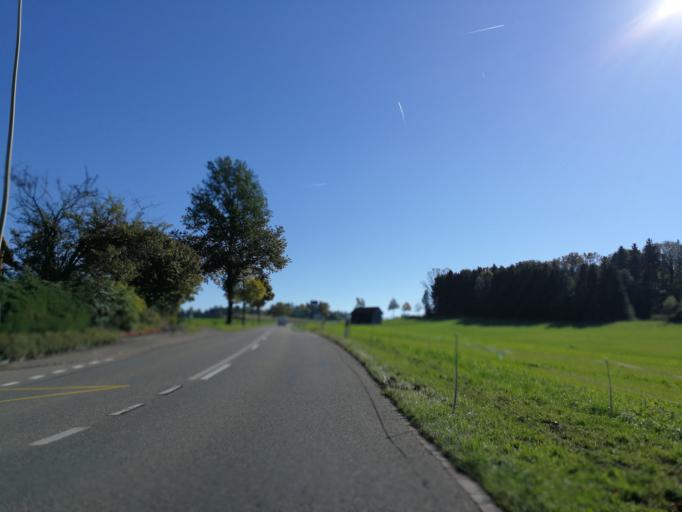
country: CH
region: Zurich
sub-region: Bezirk Meilen
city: Oetwil am See
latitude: 47.2691
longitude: 8.7141
